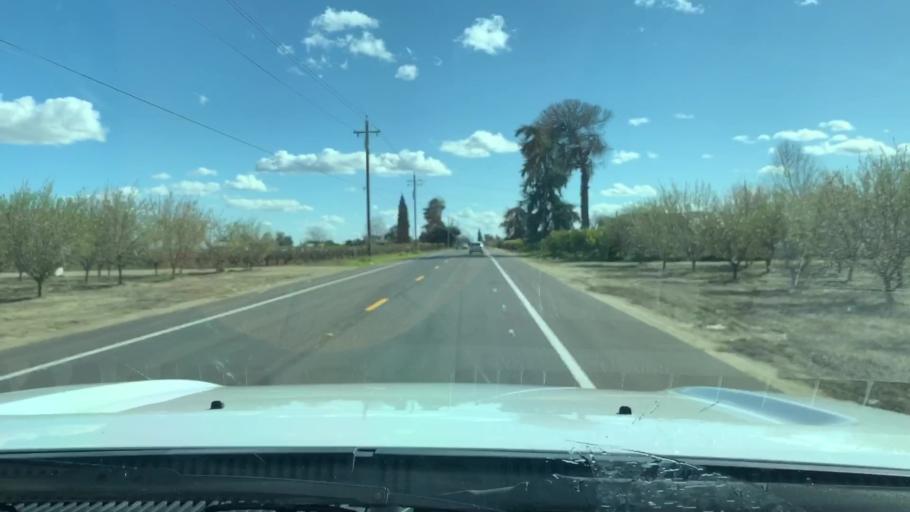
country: US
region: California
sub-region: Fresno County
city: Fowler
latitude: 36.5877
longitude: -119.6825
